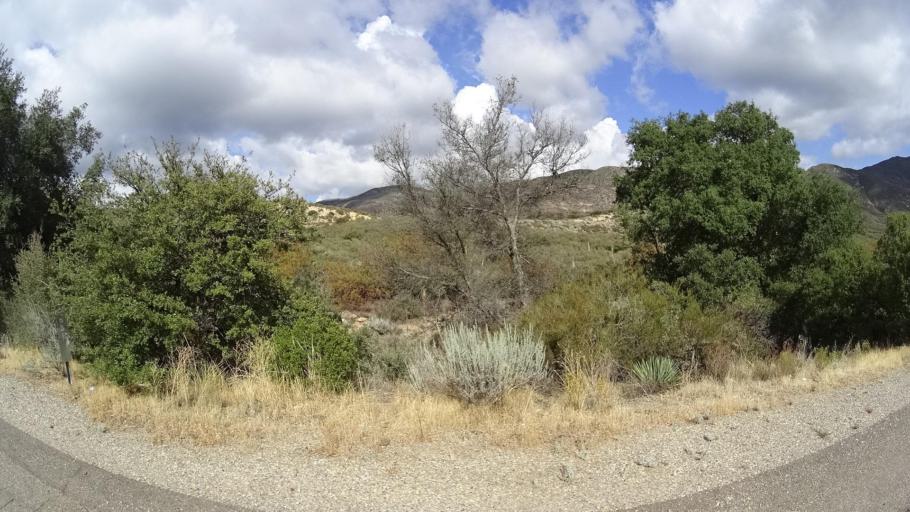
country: US
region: California
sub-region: San Diego County
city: Pine Valley
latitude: 32.8036
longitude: -116.5047
